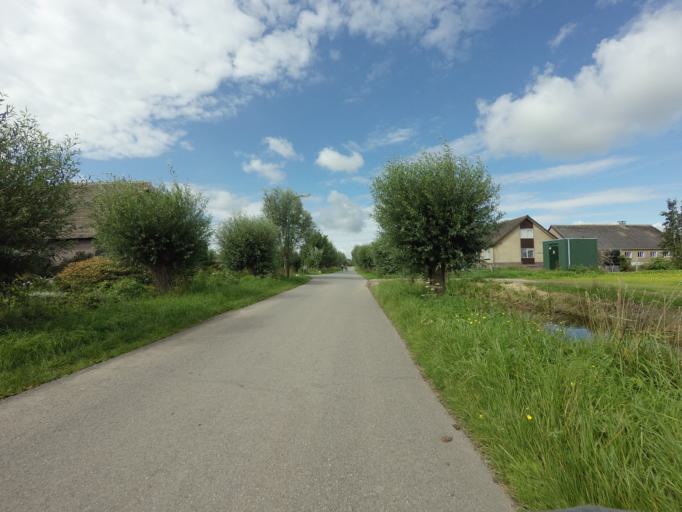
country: NL
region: Utrecht
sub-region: Gemeente Oudewater
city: Oudewater
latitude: 52.0034
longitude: 4.8443
